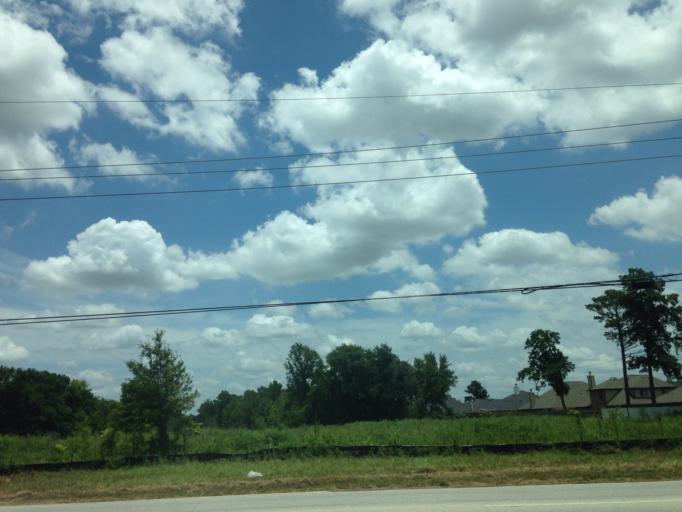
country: US
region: Texas
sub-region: Harris County
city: Spring
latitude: 30.0471
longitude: -95.4914
